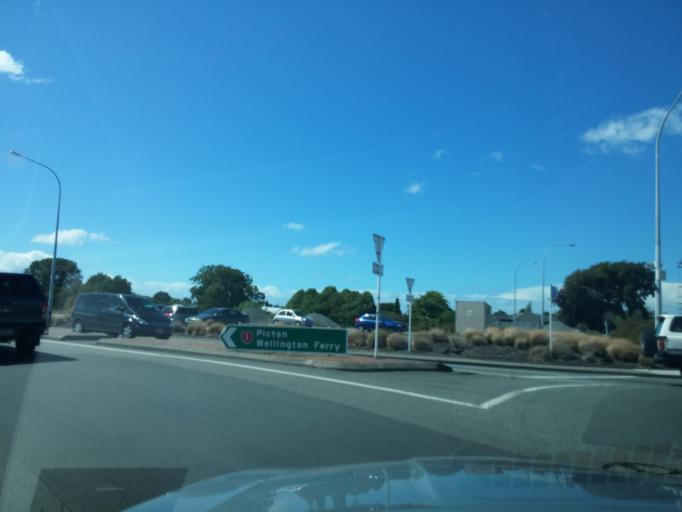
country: NZ
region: Marlborough
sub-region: Marlborough District
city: Blenheim
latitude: -41.5080
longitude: 173.9592
